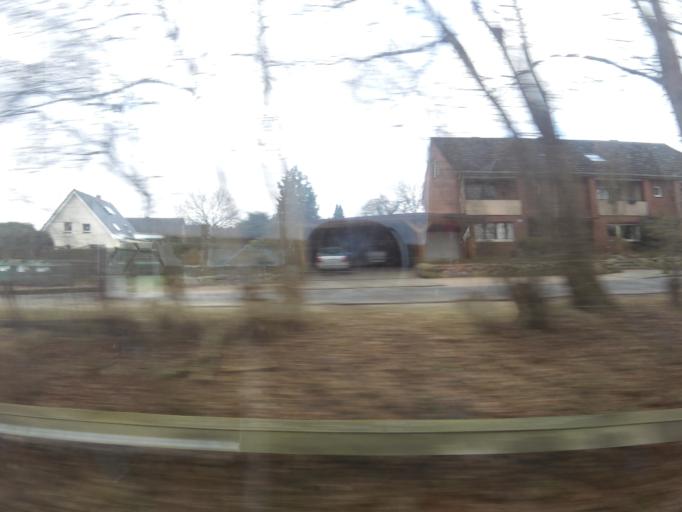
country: DE
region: Hamburg
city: Harburg
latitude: 53.4240
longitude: 10.0176
